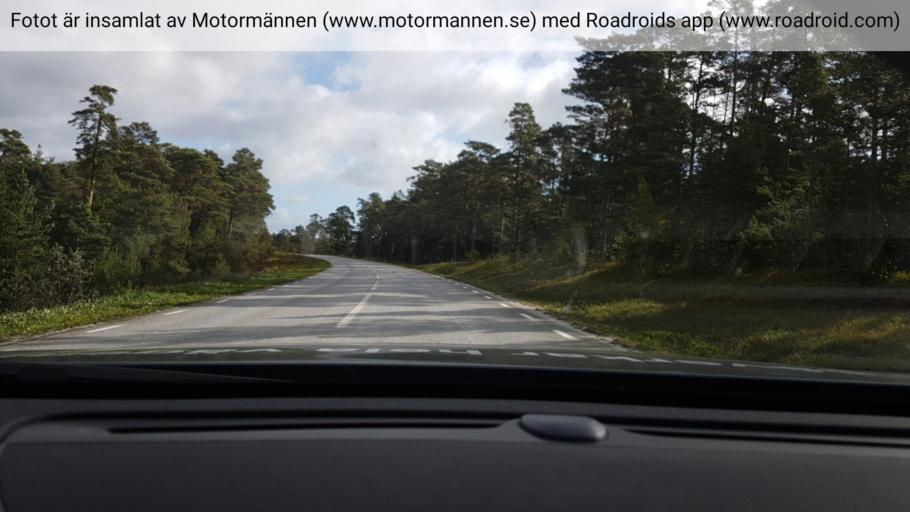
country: SE
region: Gotland
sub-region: Gotland
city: Slite
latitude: 57.8395
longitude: 18.9497
